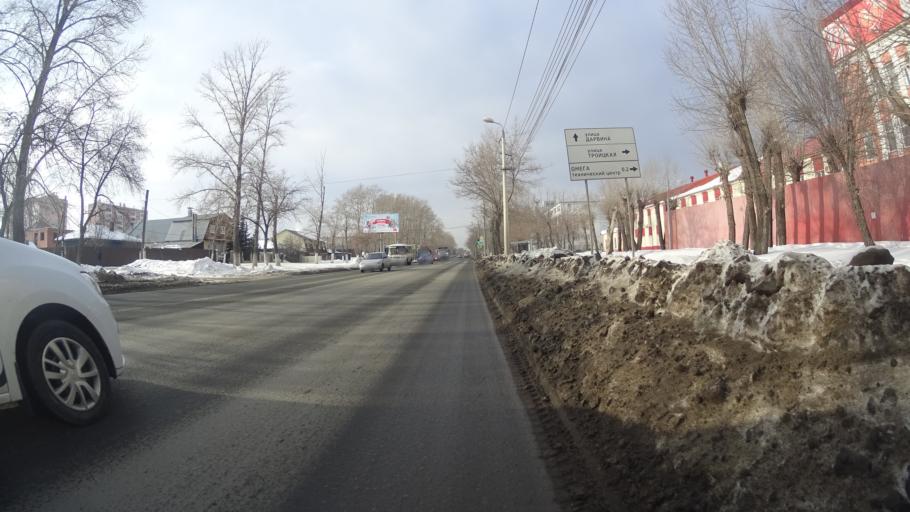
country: RU
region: Chelyabinsk
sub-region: Gorod Chelyabinsk
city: Chelyabinsk
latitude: 55.1234
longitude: 61.3741
